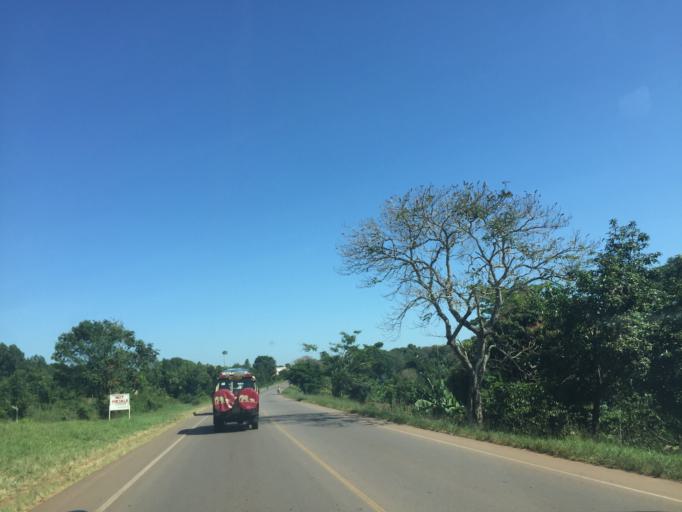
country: UG
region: Central Region
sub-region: Luwero District
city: Wobulenzi
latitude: 0.7581
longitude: 32.5138
